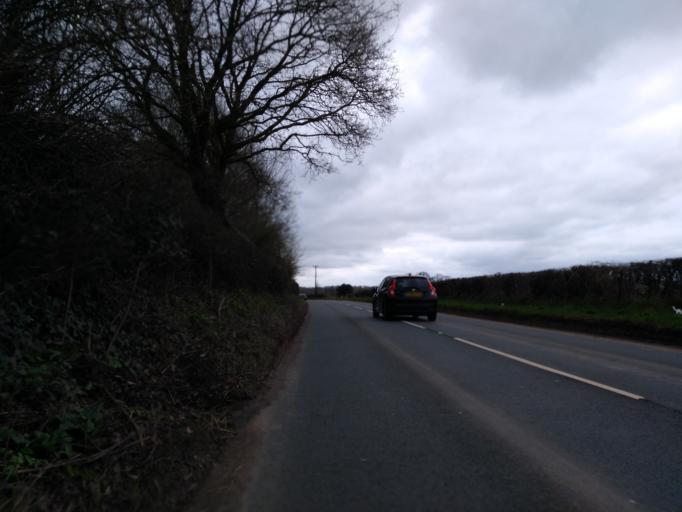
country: GB
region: England
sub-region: Devon
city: Crediton
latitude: 50.7773
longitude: -3.6105
